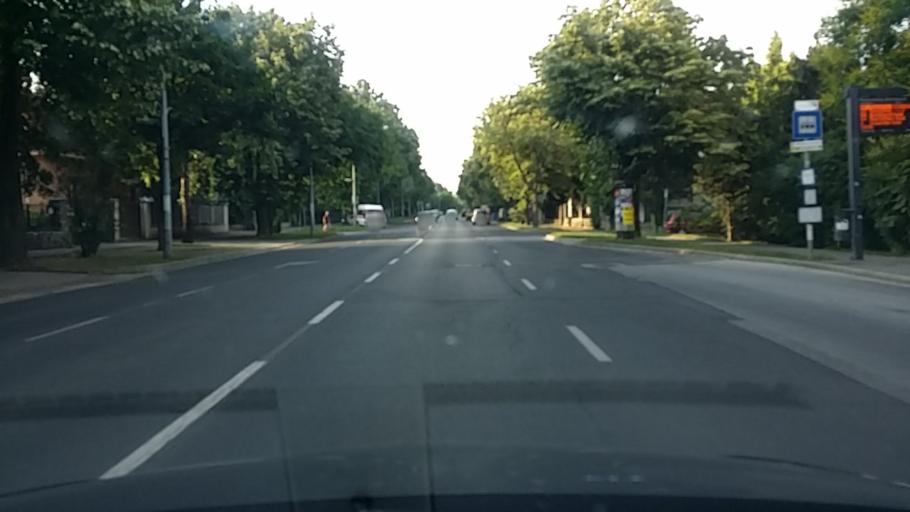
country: HU
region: Borsod-Abauj-Zemplen
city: Miskolc
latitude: 48.0861
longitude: 20.7855
